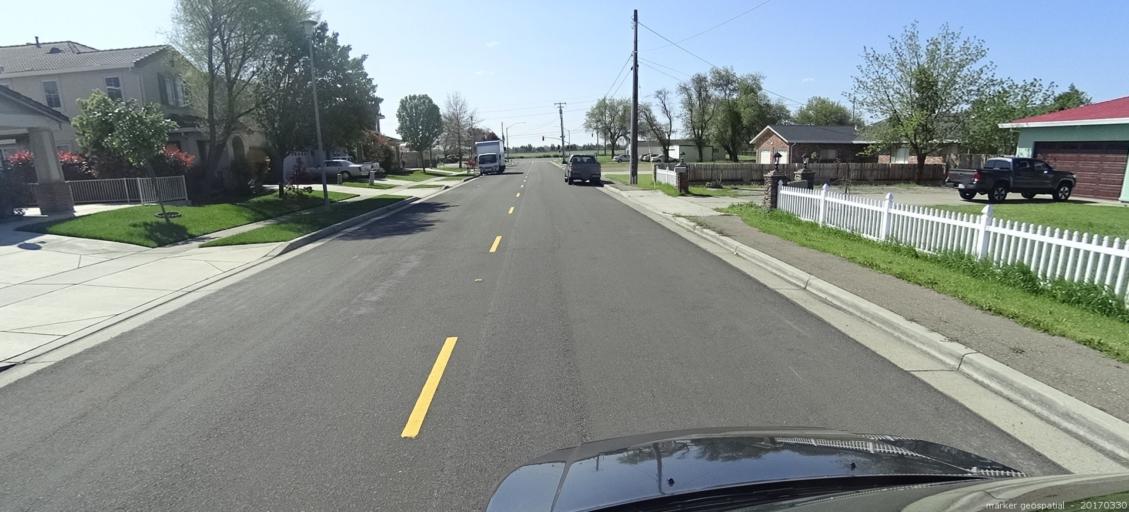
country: US
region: California
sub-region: Sacramento County
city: Laguna
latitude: 38.4397
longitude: -121.4132
